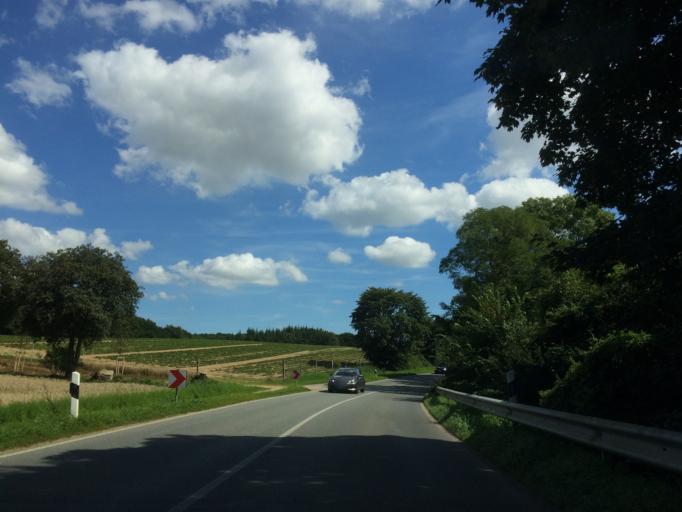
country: DE
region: Schleswig-Holstein
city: Eutin
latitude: 54.1612
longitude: 10.5875
